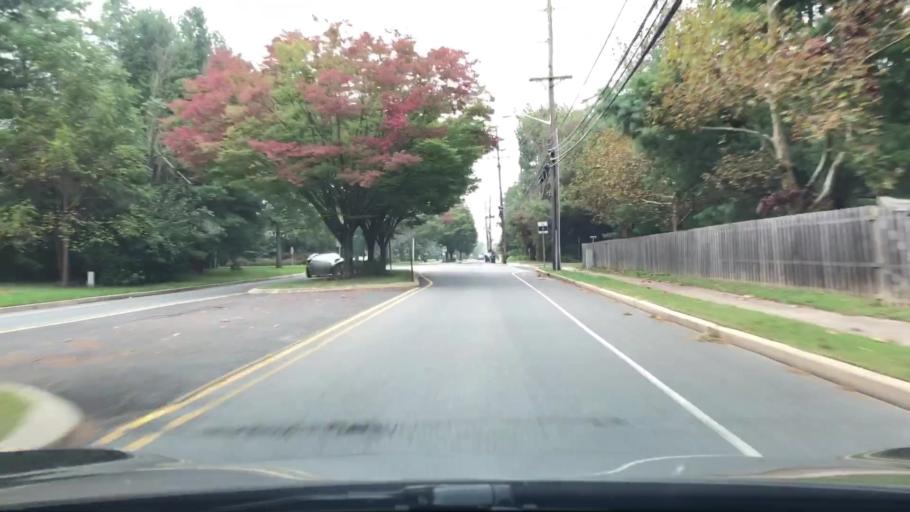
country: US
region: New Jersey
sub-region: Mercer County
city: Lawrenceville
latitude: 40.2990
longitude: -74.7526
